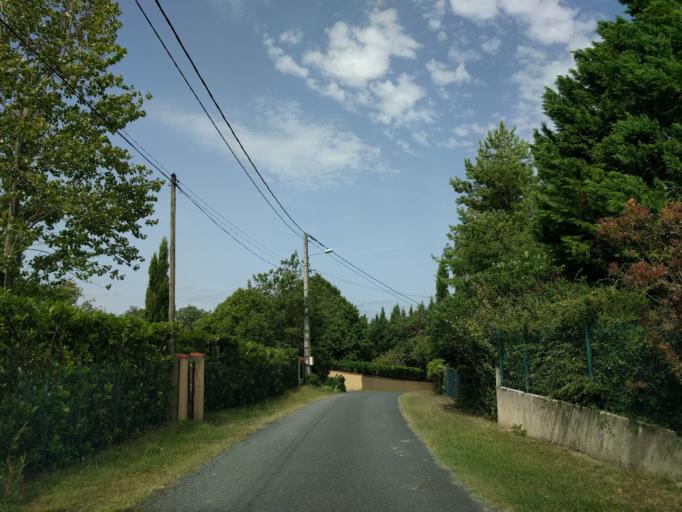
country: FR
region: Midi-Pyrenees
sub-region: Departement du Tarn
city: Saix
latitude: 43.6362
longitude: 2.2002
